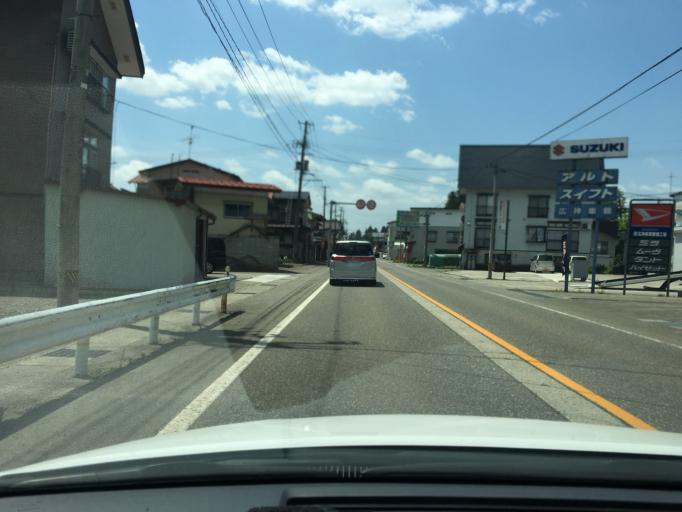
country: JP
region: Niigata
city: Tochio-honcho
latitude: 37.2966
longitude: 138.9926
